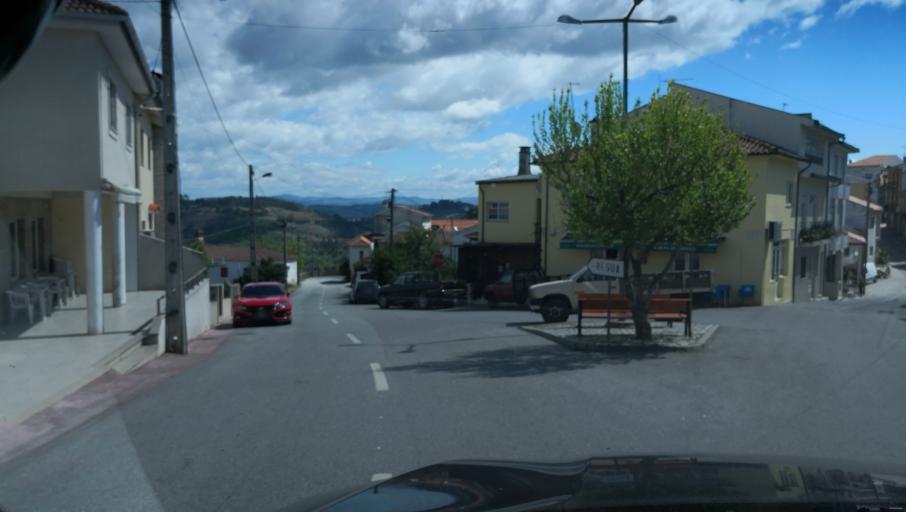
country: PT
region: Vila Real
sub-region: Vila Real
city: Vila Real
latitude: 41.2578
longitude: -7.7339
